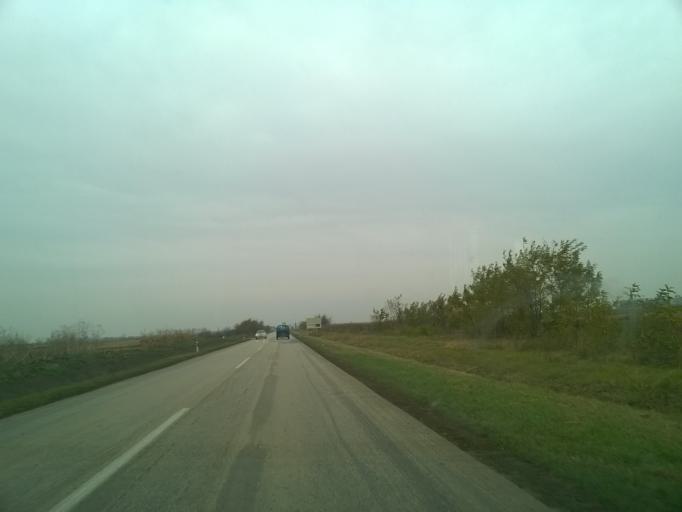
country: RS
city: Crepaja
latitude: 44.9849
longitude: 20.6446
